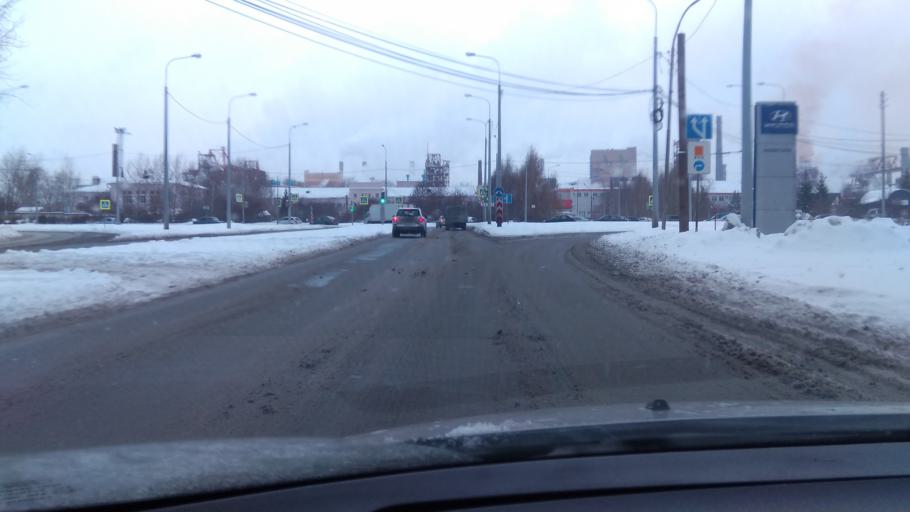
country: RU
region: Sverdlovsk
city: Nizhniy Tagil
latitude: 57.9081
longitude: 60.0093
